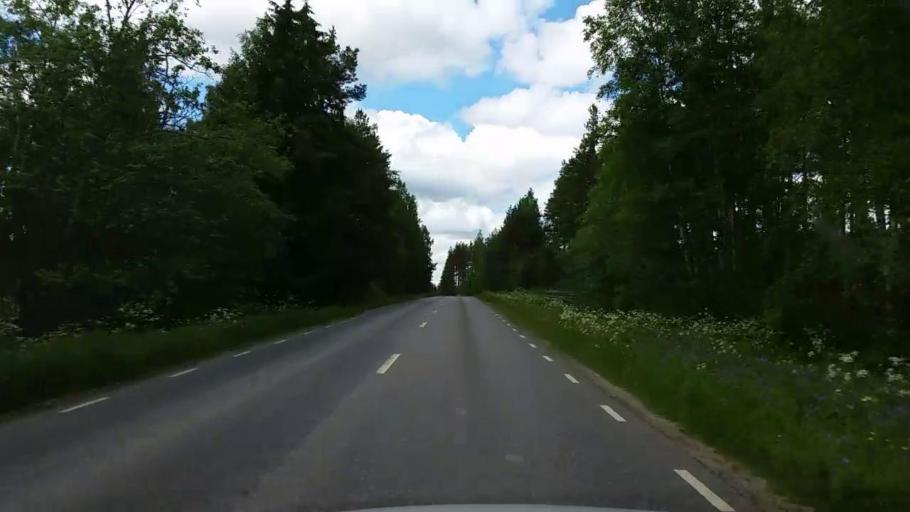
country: SE
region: Gaevleborg
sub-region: Ovanakers Kommun
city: Alfta
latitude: 61.3803
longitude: 16.0502
